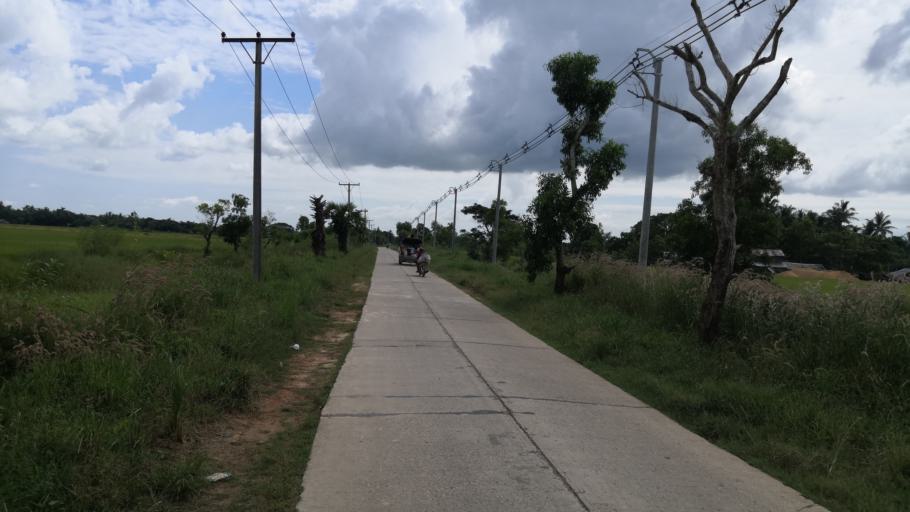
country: MM
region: Yangon
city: Kanbe
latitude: 16.4380
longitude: 96.1577
